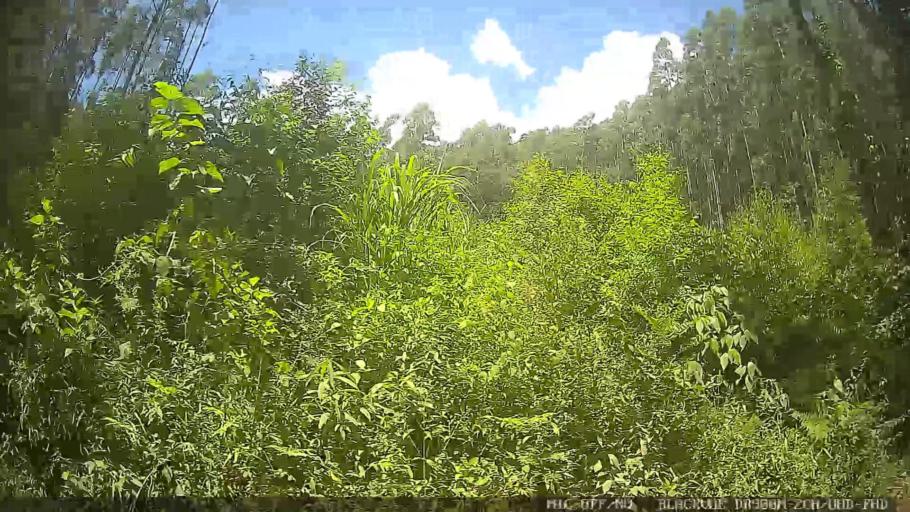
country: BR
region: Minas Gerais
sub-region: Extrema
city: Extrema
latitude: -22.8867
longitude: -46.2949
